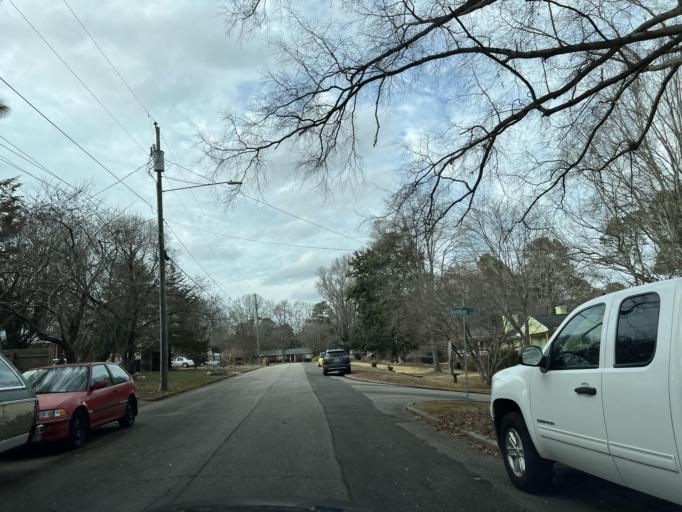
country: US
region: North Carolina
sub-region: Wake County
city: West Raleigh
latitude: 35.7732
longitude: -78.7069
